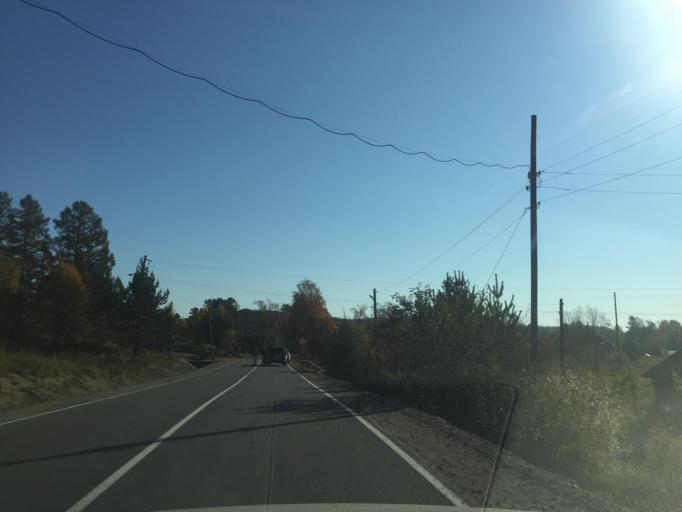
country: RU
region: Leningrad
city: Kuznechnoye
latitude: 61.3025
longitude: 29.8845
